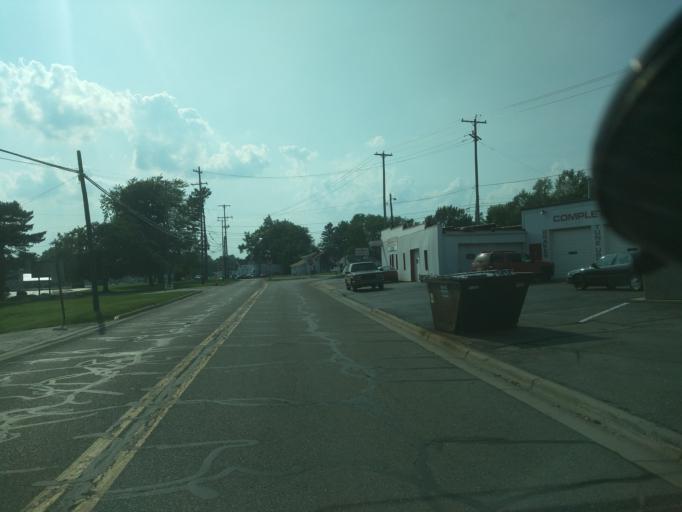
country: US
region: Michigan
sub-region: Jackson County
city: Jackson
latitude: 42.2543
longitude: -84.4374
